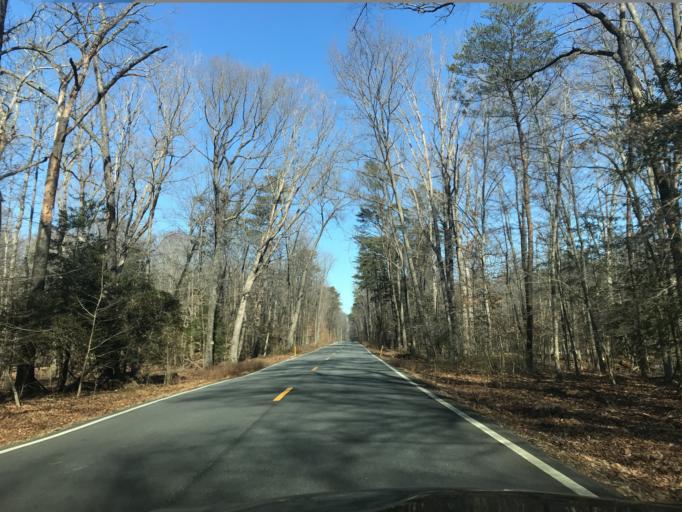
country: US
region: Virginia
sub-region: Prince William County
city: Quantico Station
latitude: 38.4896
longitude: -77.2561
